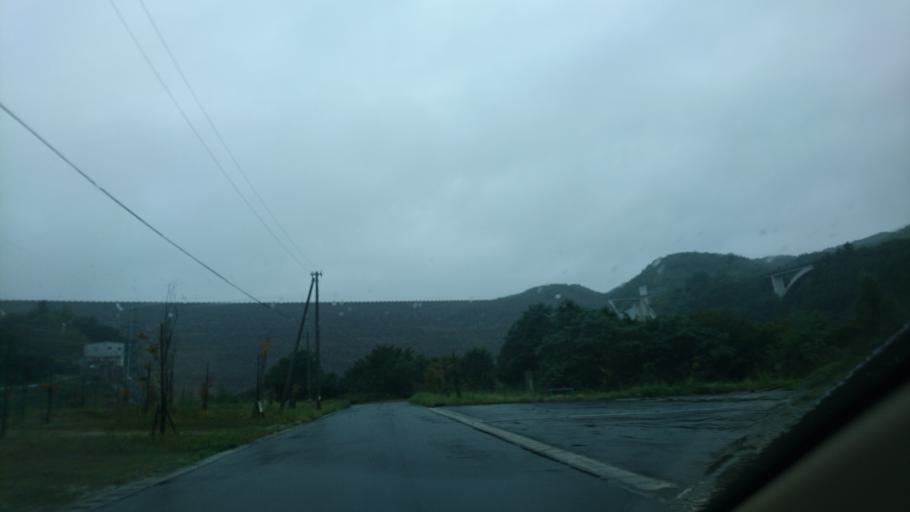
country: JP
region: Iwate
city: Mizusawa
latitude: 39.1211
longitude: 140.9260
